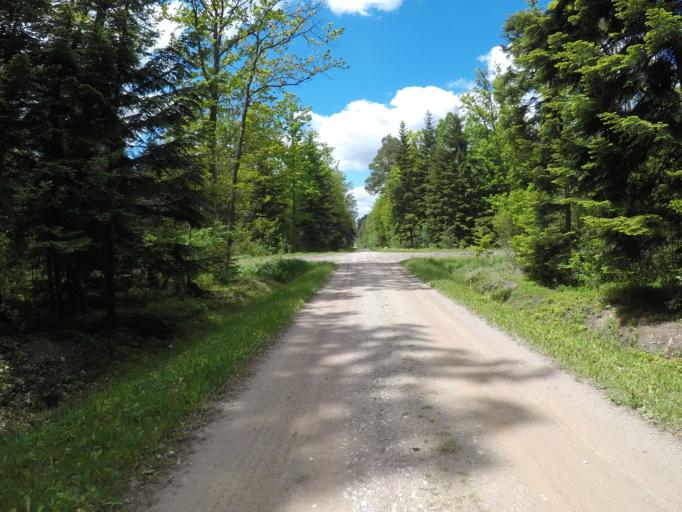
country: PL
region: Swietokrzyskie
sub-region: Powiat kielecki
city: Kostomloty Pierwsze
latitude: 50.9310
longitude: 20.6354
